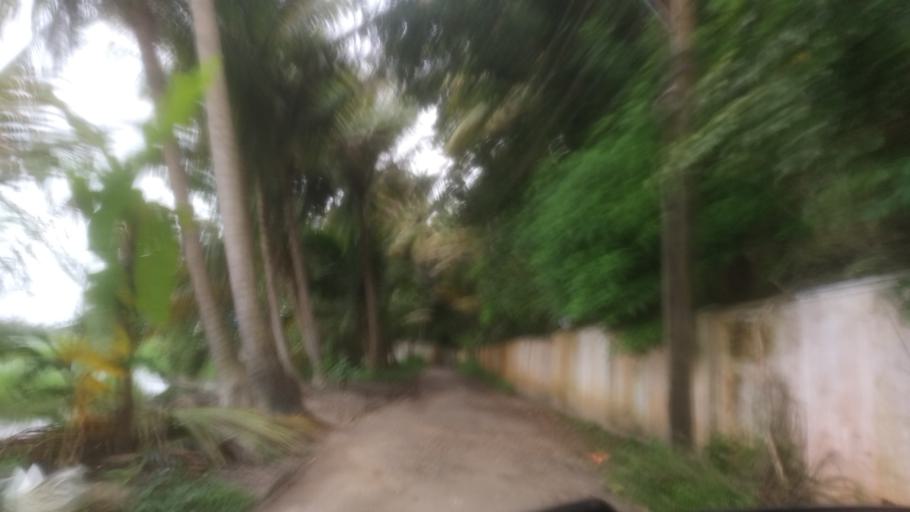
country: IN
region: Kerala
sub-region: Ernakulam
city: Elur
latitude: 10.0960
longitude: 76.2102
